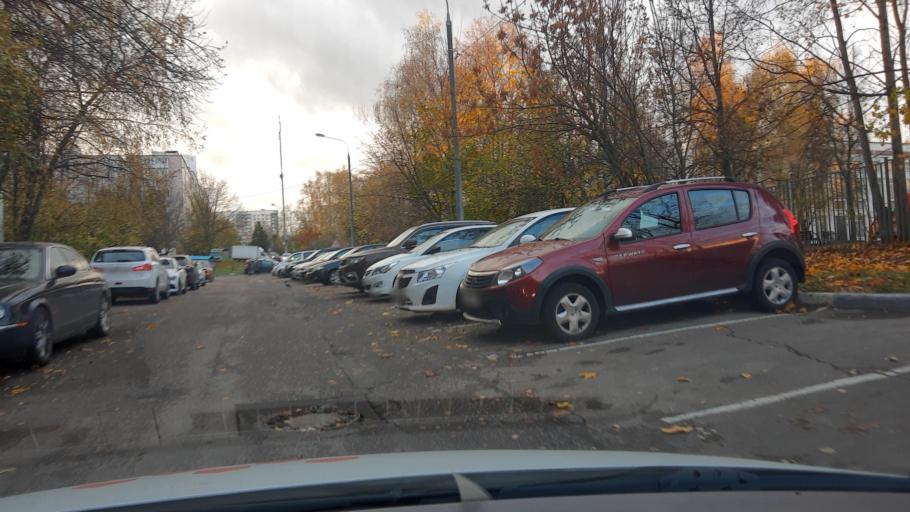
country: RU
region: Moscow
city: Yasenevo
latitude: 55.6052
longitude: 37.5530
